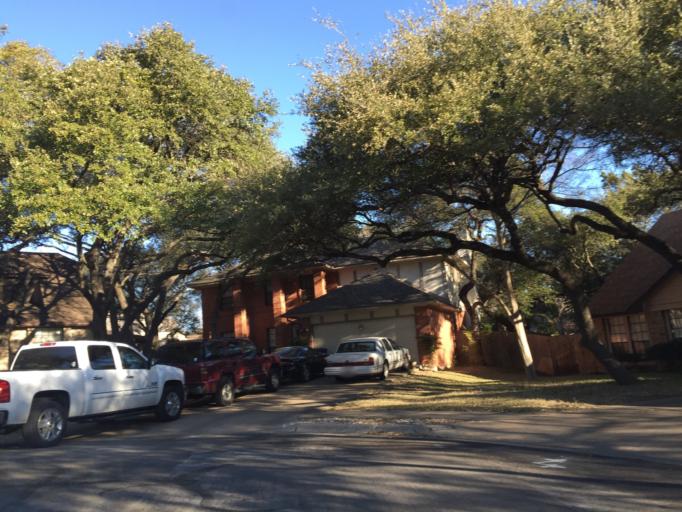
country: US
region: Texas
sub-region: Williamson County
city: Jollyville
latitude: 30.4435
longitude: -97.7670
